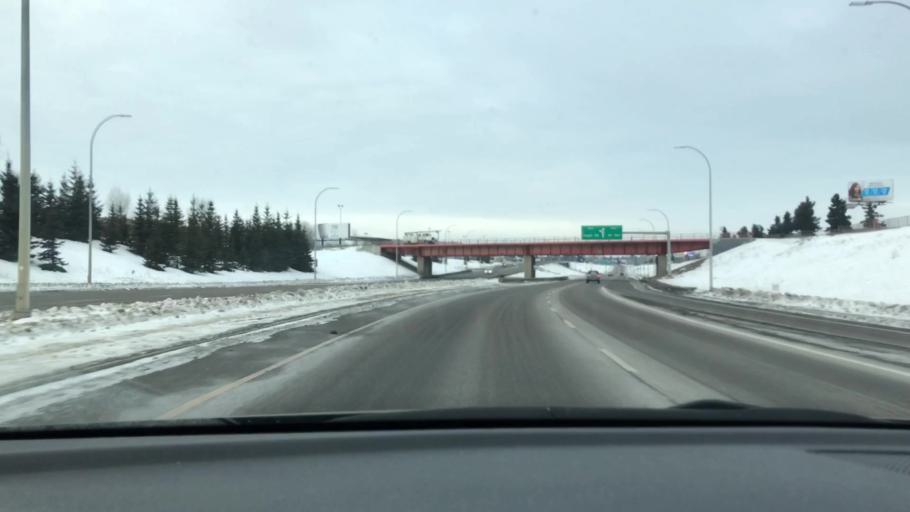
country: CA
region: Alberta
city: Edmonton
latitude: 53.5143
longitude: -113.4221
